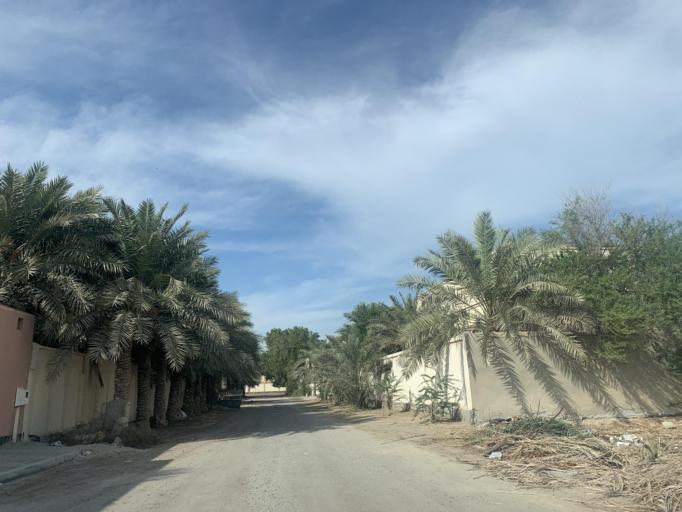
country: BH
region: Central Governorate
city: Madinat Hamad
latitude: 26.1220
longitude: 50.4679
